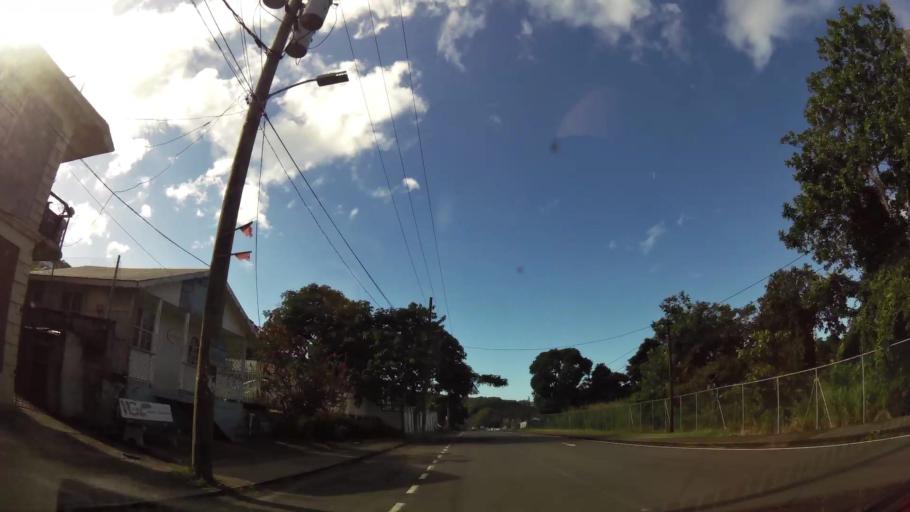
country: DM
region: Saint John
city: Portsmouth
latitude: 15.5556
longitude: -61.4588
